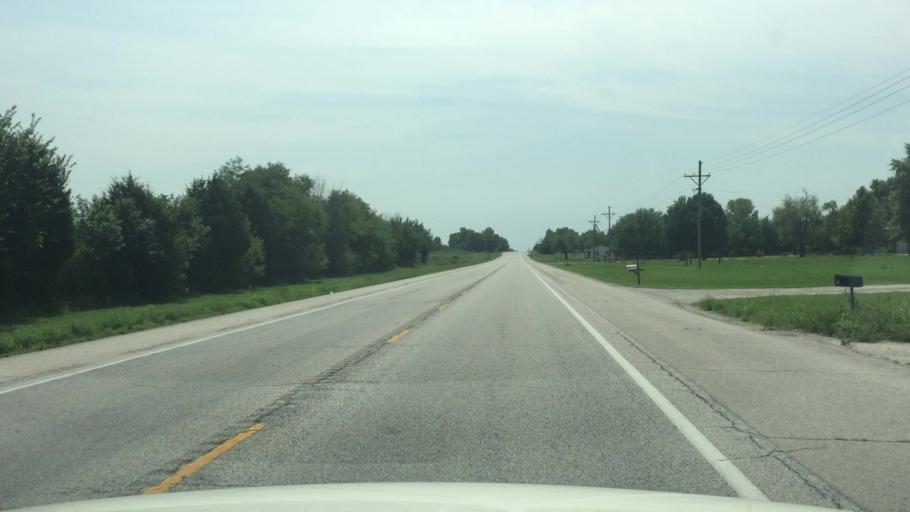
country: US
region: Kansas
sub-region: Cherokee County
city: Galena
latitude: 37.1105
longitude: -94.7044
